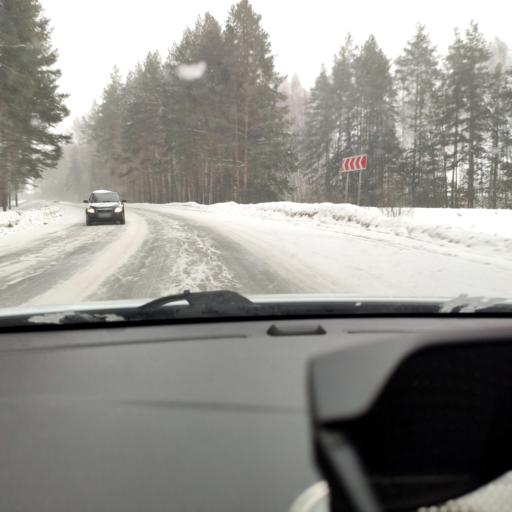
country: RU
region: Tatarstan
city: Vysokaya Gora
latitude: 55.9043
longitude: 49.2686
